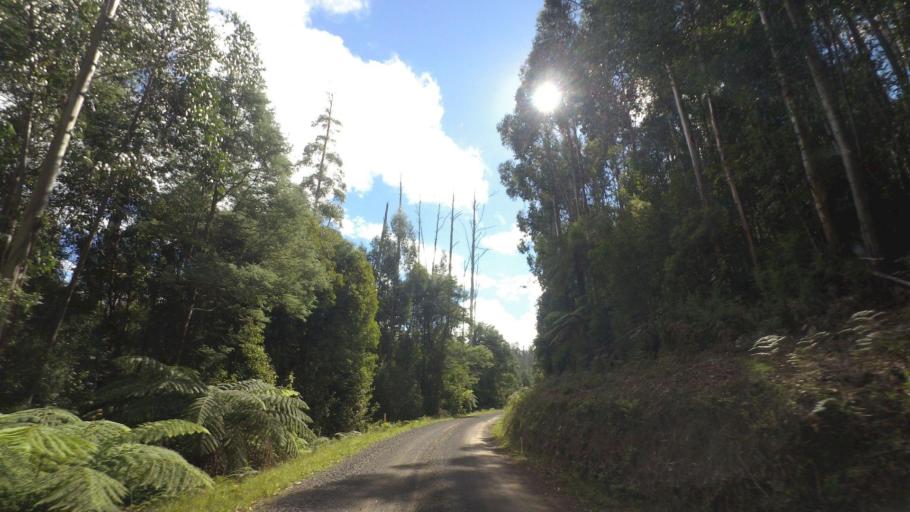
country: AU
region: Victoria
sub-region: Cardinia
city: Bunyip
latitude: -37.9559
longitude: 145.8191
